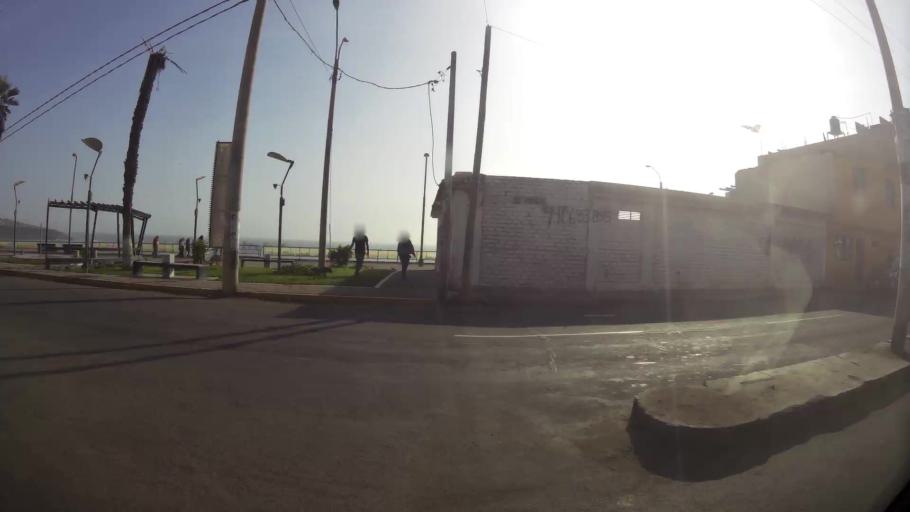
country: PE
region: Lima
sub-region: Huaura
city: Huacho
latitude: -11.1124
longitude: -77.6125
